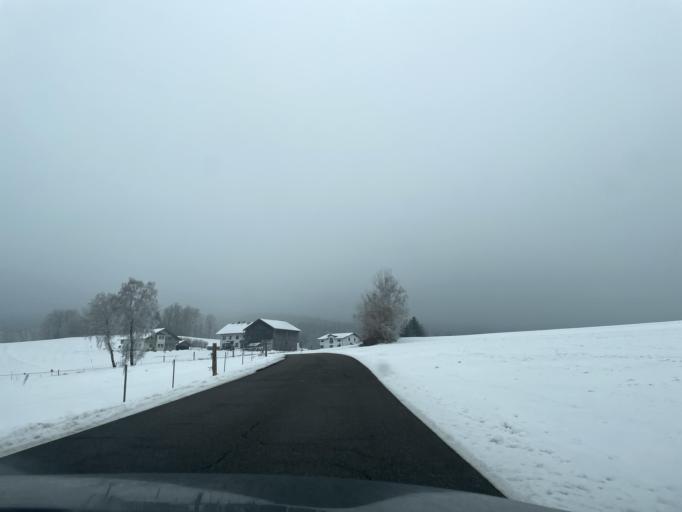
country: DE
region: Bavaria
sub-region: Lower Bavaria
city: Achslach
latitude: 49.0111
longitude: 12.9042
